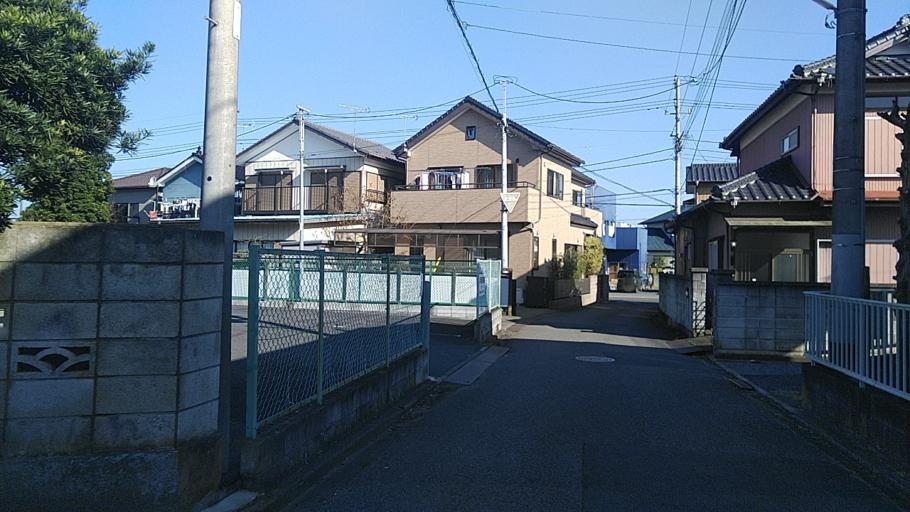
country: JP
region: Chiba
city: Katori-shi
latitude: 35.8939
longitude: 140.4911
